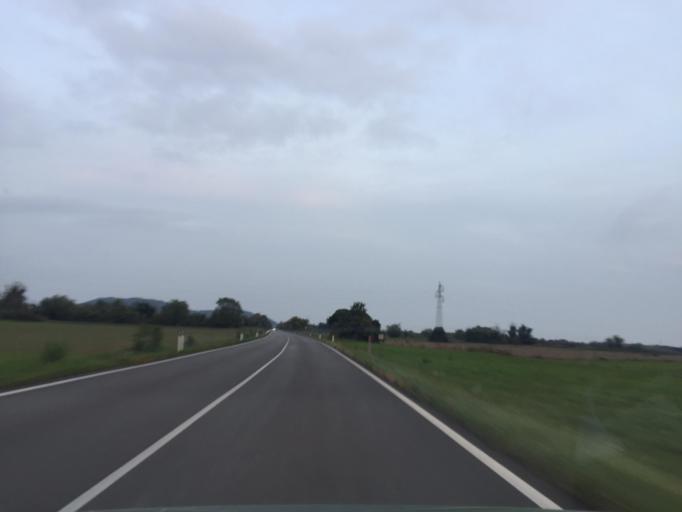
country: IT
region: Friuli Venezia Giulia
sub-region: Provincia di Pordenone
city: Arba
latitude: 46.1659
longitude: 12.7723
